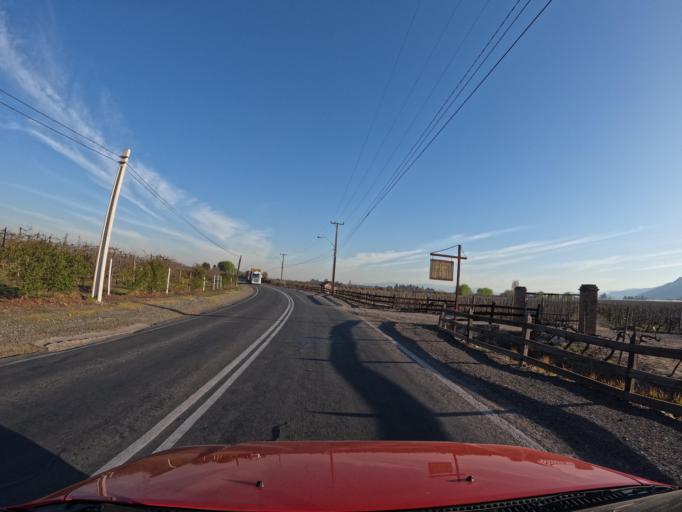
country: CL
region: Maule
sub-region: Provincia de Curico
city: Rauco
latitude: -34.9066
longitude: -71.2789
